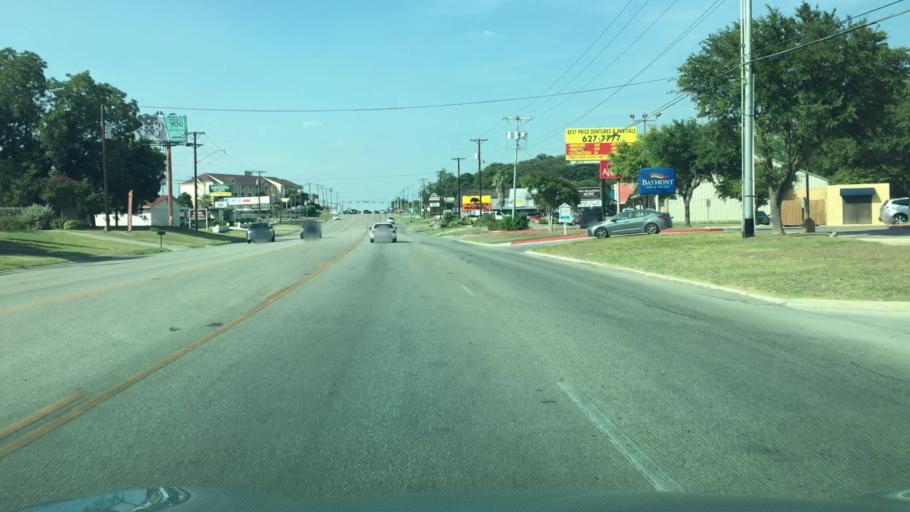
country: US
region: Texas
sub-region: Comal County
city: New Braunfels
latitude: 29.6986
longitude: -98.0984
